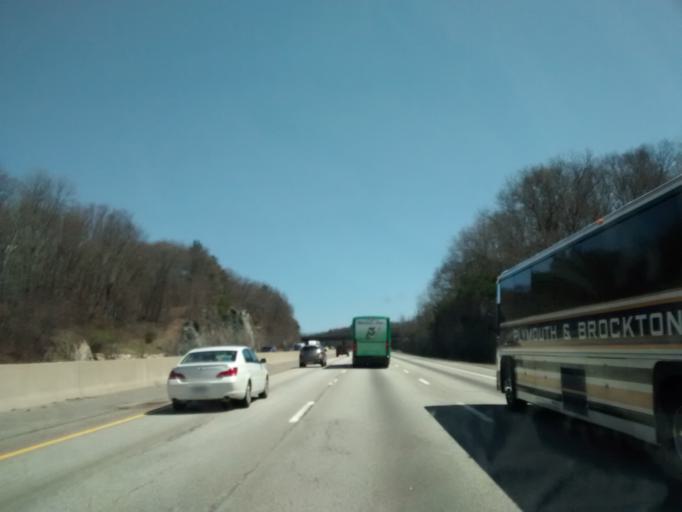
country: US
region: Massachusetts
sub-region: Worcester County
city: Grafton
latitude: 42.2269
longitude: -71.6740
